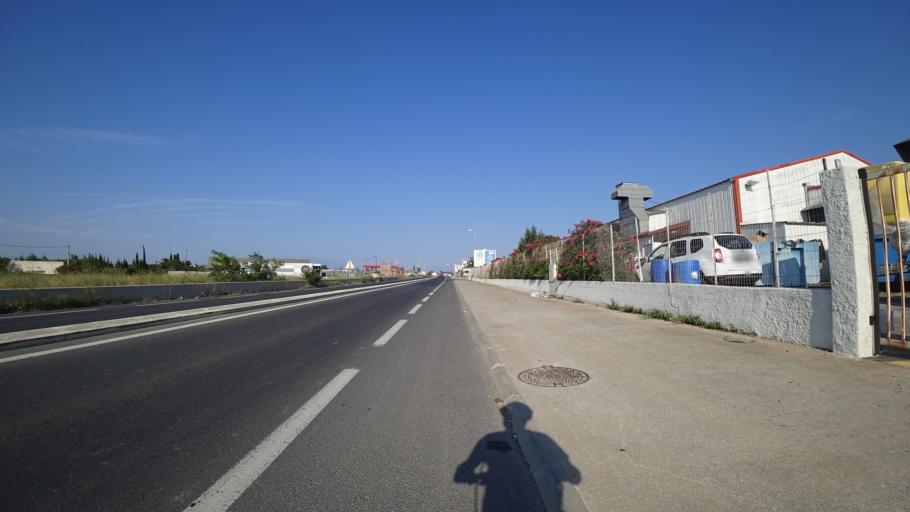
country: FR
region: Languedoc-Roussillon
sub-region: Departement des Pyrenees-Orientales
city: Pia
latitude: 42.7275
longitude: 2.9034
